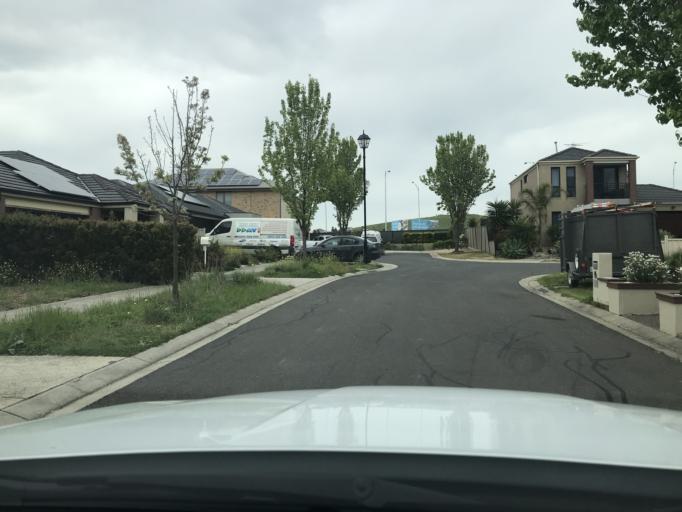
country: AU
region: Victoria
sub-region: Hume
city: Roxburgh Park
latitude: -37.6073
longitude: 144.9128
